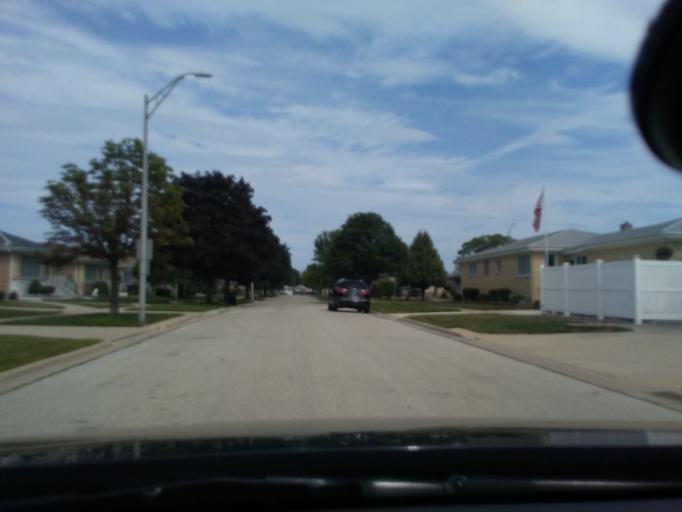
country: US
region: Illinois
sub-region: Cook County
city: Norridge
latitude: 41.9692
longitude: -87.8449
